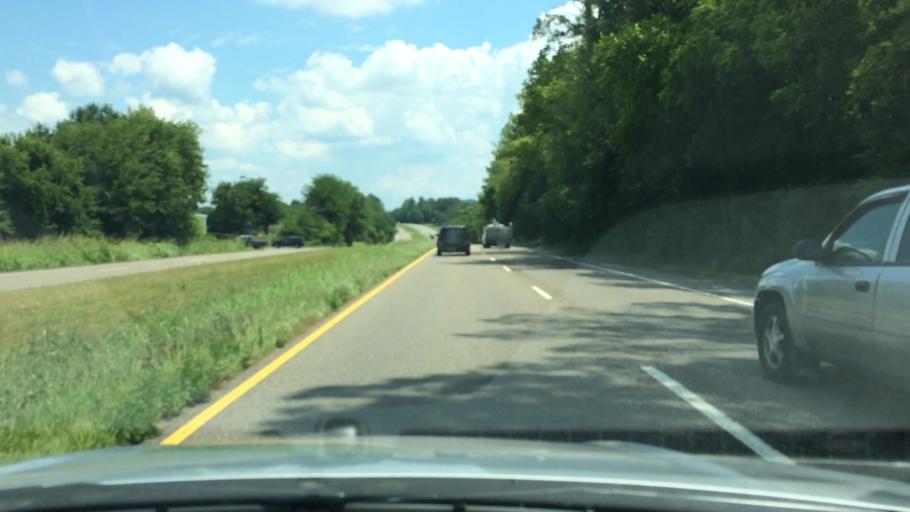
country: US
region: Tennessee
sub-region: Knox County
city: Mascot
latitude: 36.0693
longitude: -83.6506
